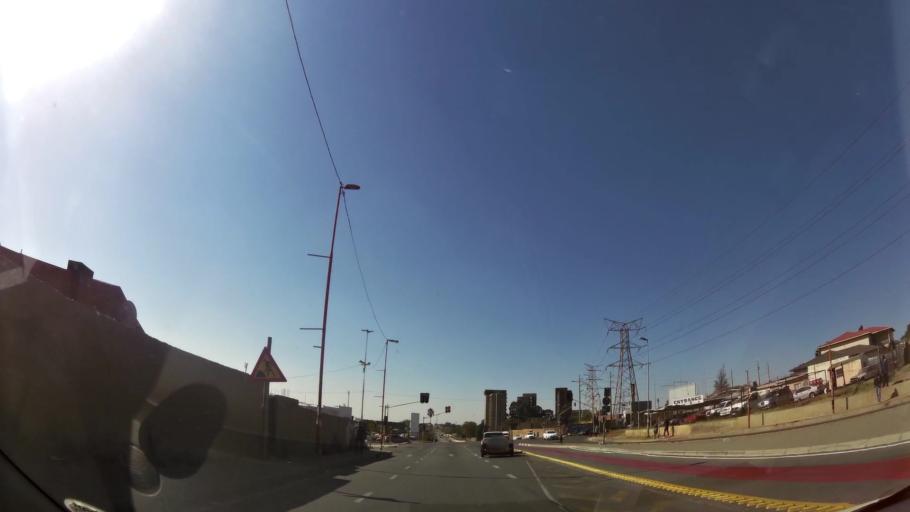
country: ZA
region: Gauteng
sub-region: City of Johannesburg Metropolitan Municipality
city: Johannesburg
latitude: -26.1864
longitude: 27.9828
